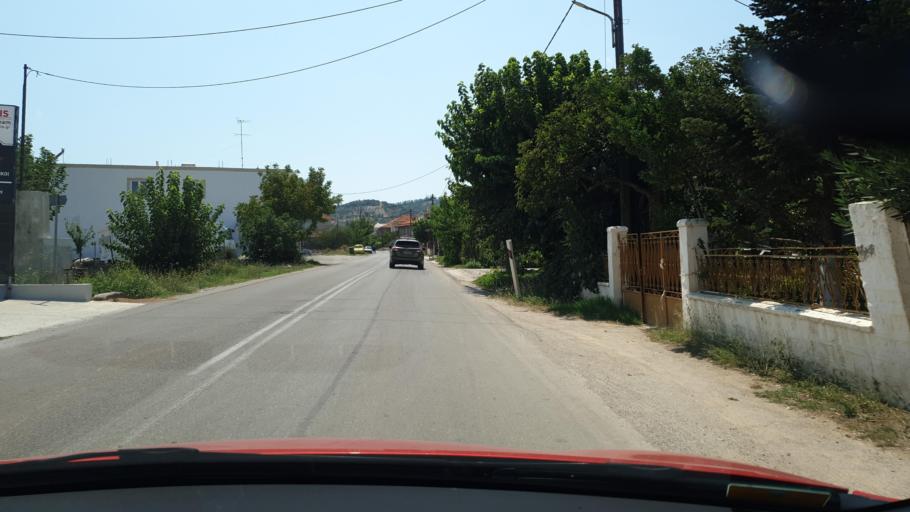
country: GR
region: Central Greece
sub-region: Nomos Evvoias
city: Aliveri
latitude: 38.4526
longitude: 24.1136
